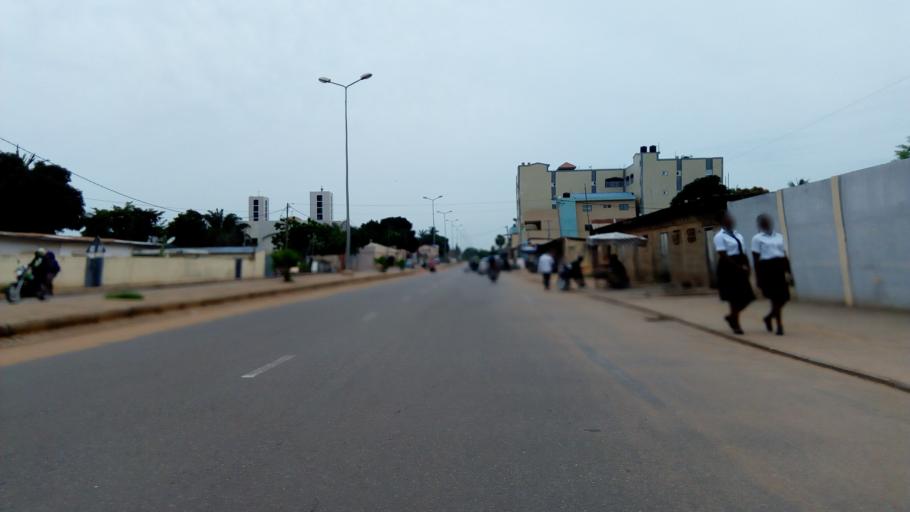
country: TG
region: Maritime
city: Lome
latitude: 6.1608
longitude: 1.2307
